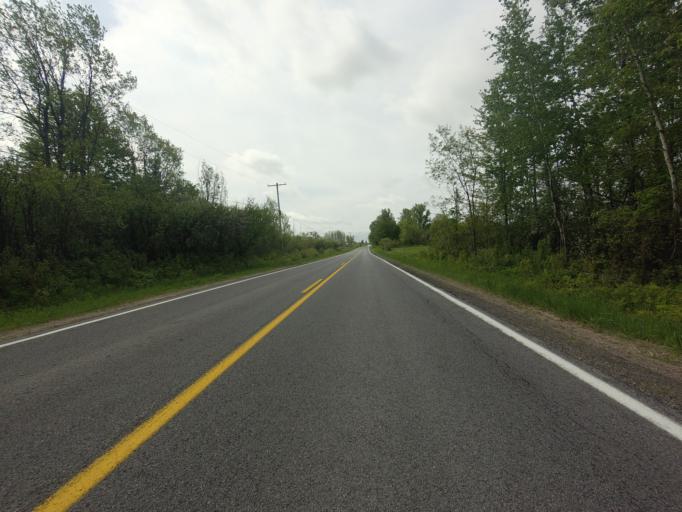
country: CA
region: Ontario
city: Cornwall
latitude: 44.7208
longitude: -74.6623
